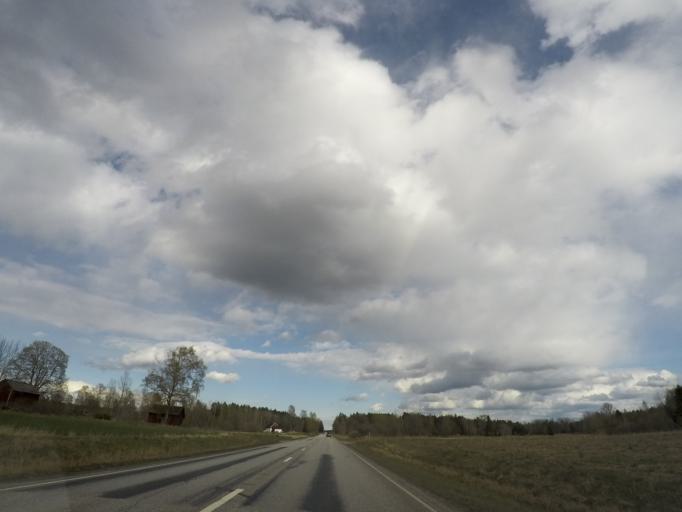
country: SE
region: Soedermanland
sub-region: Eskilstuna Kommun
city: Hallbybrunn
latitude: 59.3202
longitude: 16.3364
